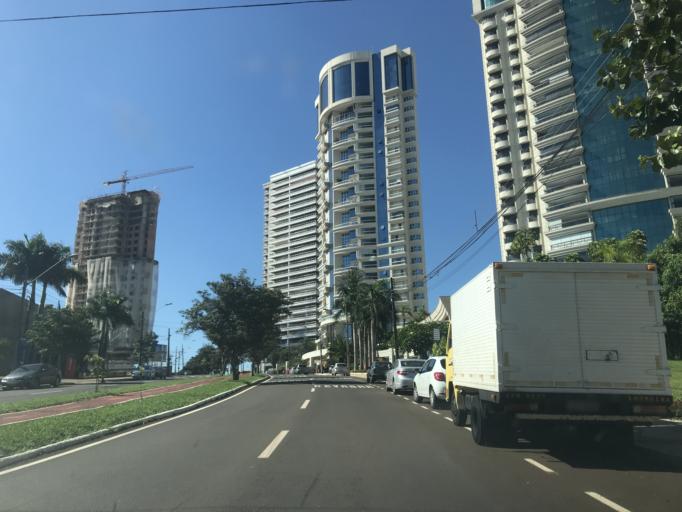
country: BR
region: Parana
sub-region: Londrina
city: Londrina
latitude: -23.3406
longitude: -51.1645
